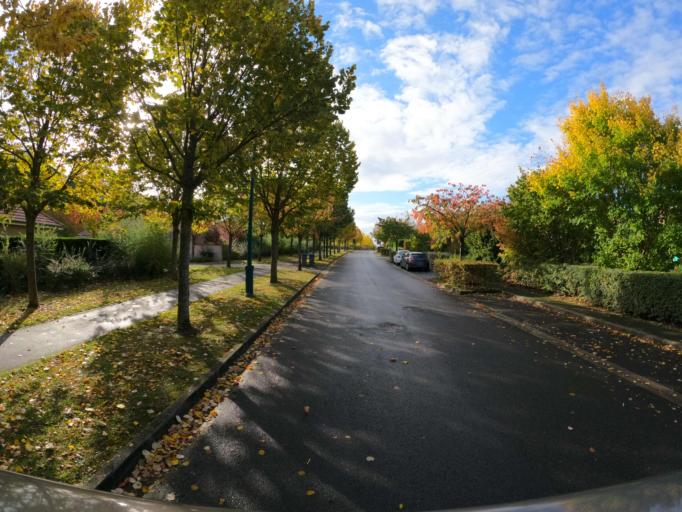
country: FR
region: Ile-de-France
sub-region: Departement de Seine-et-Marne
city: Magny-le-Hongre
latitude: 48.8648
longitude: 2.8235
